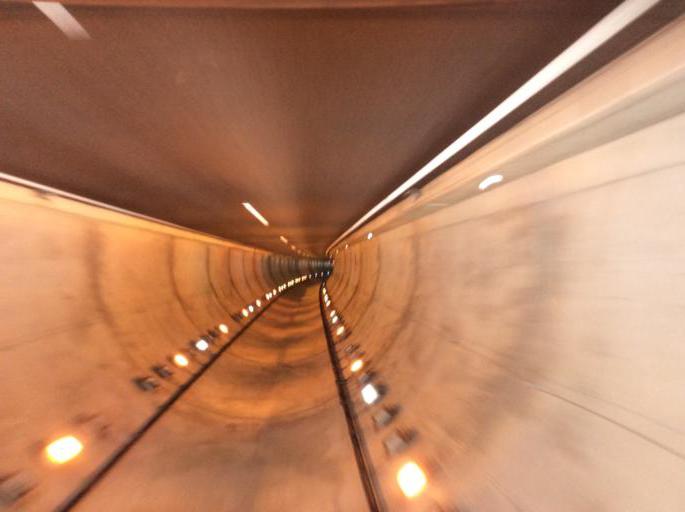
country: JP
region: Fukushima
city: Iwaki
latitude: 37.0864
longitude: 140.7872
